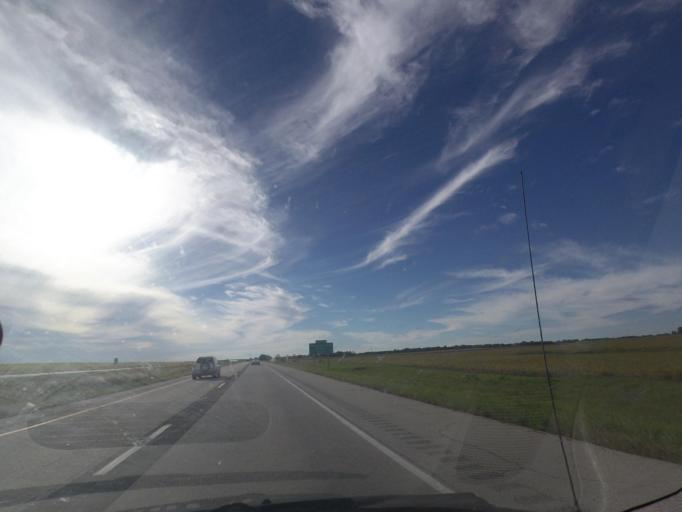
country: US
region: Illinois
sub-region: Sangamon County
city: Riverton
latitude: 39.8386
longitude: -89.3914
